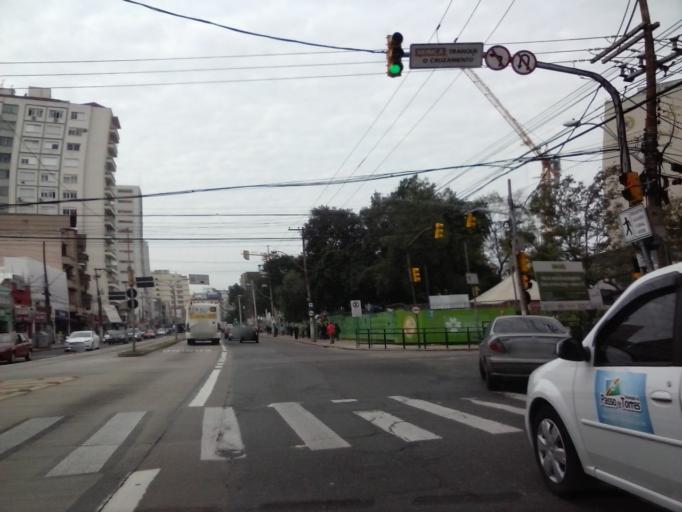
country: BR
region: Rio Grande do Sul
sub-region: Porto Alegre
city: Porto Alegre
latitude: -30.0370
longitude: -51.2085
